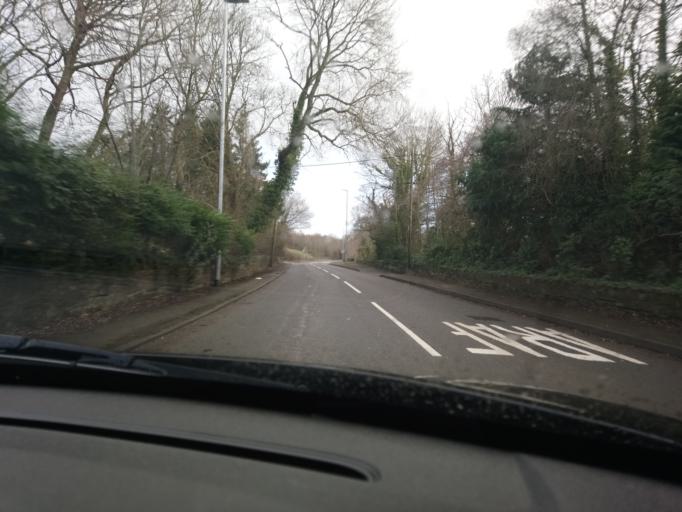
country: GB
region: Wales
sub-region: Wrexham
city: Ruabon
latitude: 52.9684
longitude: -3.0614
